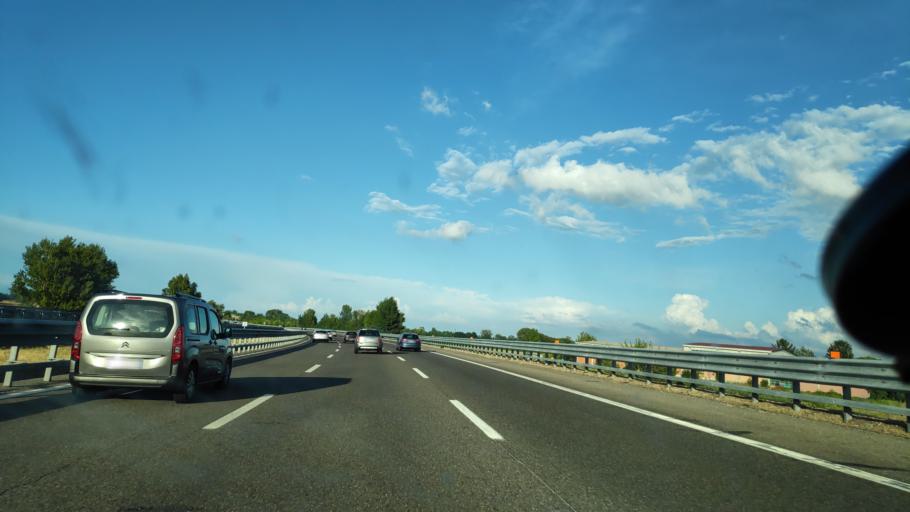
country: IT
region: Piedmont
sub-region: Provincia di Alessandria
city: Castelnuovo Scrivia
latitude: 44.9542
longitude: 8.8727
